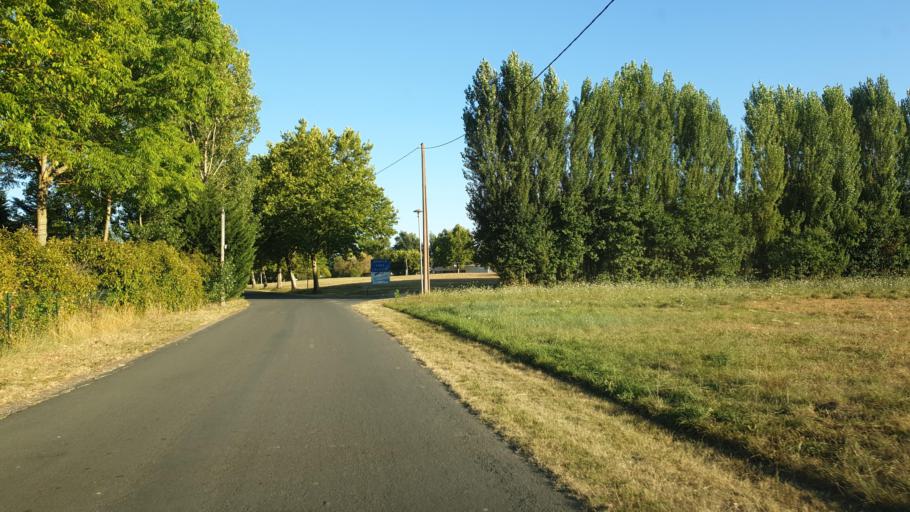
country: FR
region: Aquitaine
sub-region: Departement du Lot-et-Garonne
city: Castelmoron-sur-Lot
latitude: 44.3898
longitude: 0.5057
